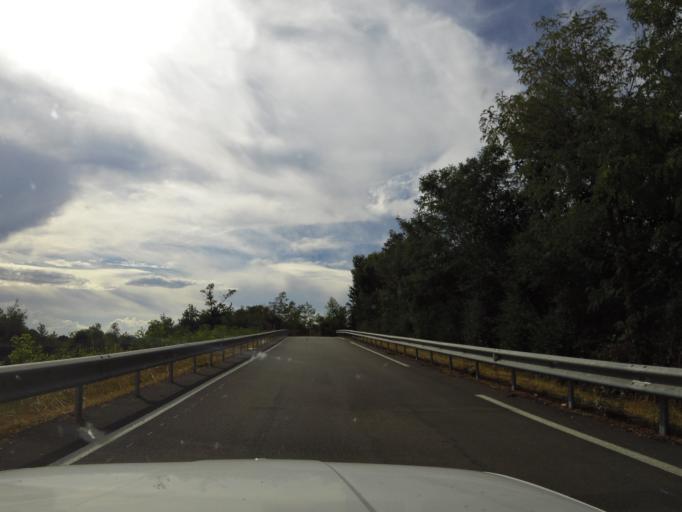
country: FR
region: Rhone-Alpes
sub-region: Departement de l'Ain
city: Saint-Jean-de-Niost
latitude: 45.8564
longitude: 5.2238
